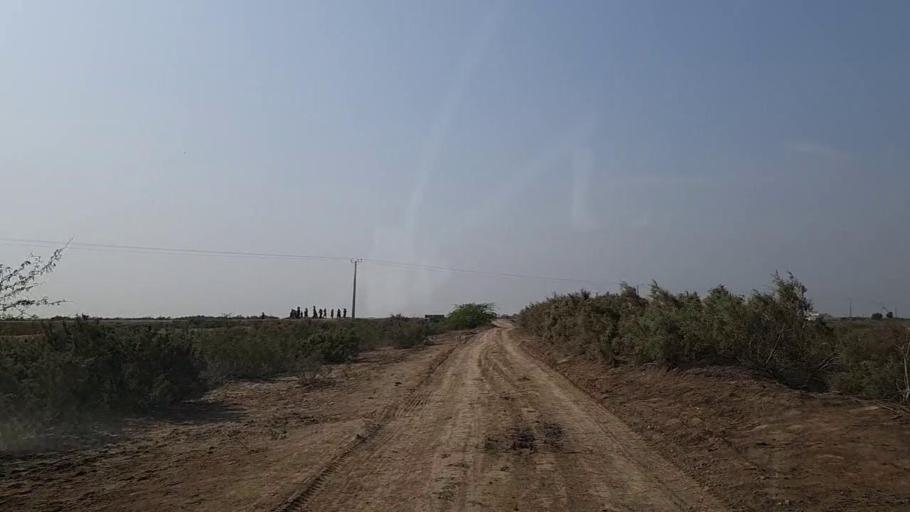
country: PK
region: Sindh
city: Gharo
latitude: 24.6735
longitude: 67.7030
